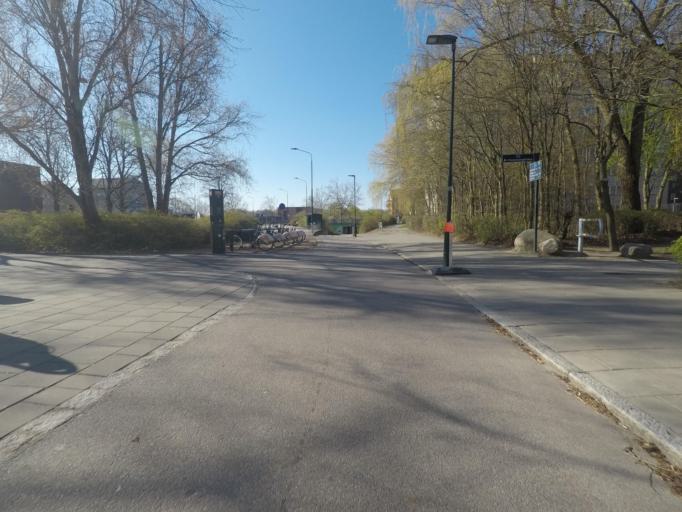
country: SE
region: Skane
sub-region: Malmo
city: Tygelsjo
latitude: 55.5597
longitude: 13.0130
